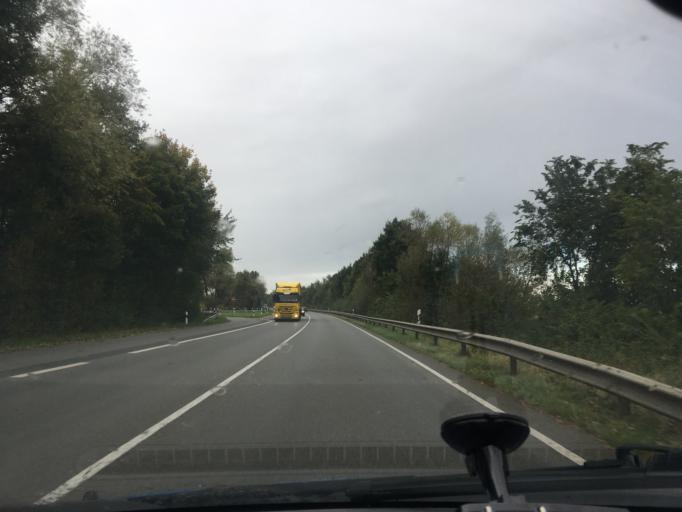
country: DE
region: Lower Saxony
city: Handorf
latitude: 53.3800
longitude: 10.3478
